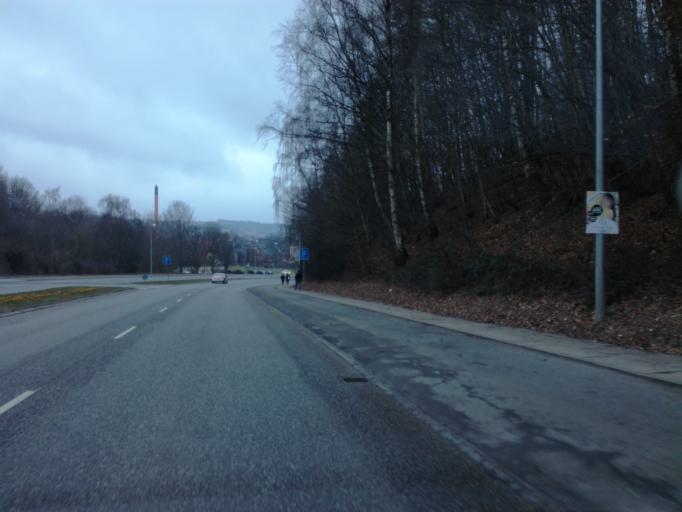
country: DK
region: South Denmark
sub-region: Vejle Kommune
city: Vejle
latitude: 55.7153
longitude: 9.5495
